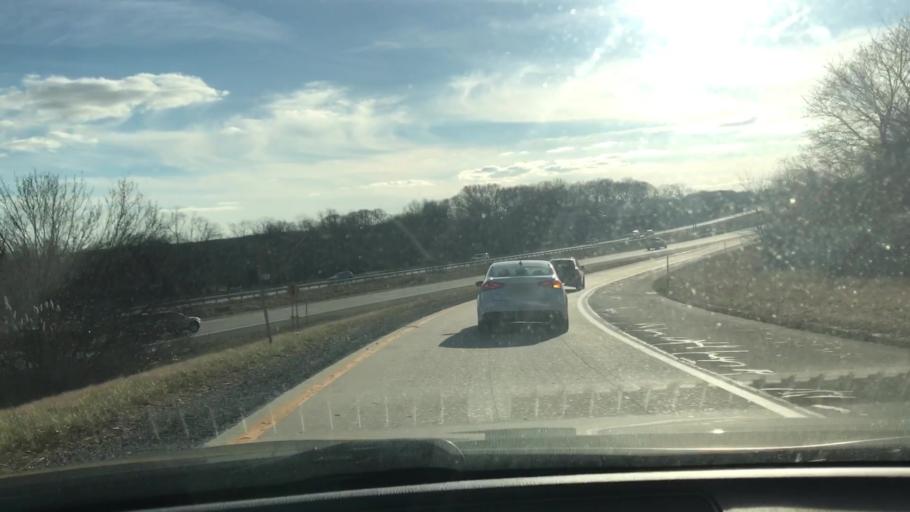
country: US
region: New York
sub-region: Suffolk County
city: Calverton
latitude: 40.9203
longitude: -72.7254
